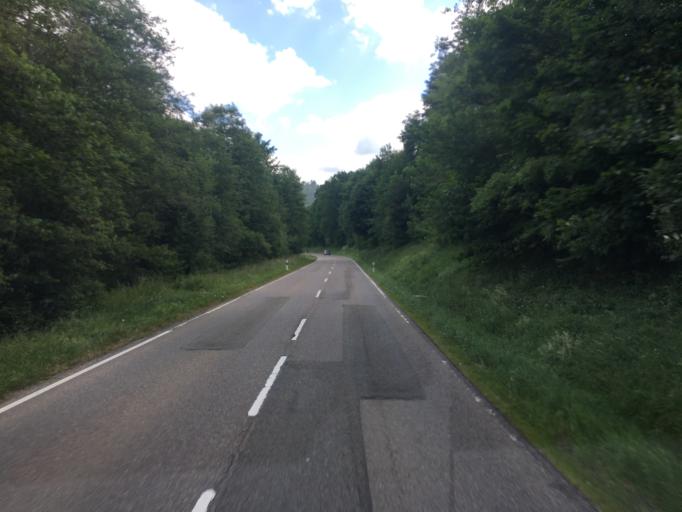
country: DE
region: Baden-Wuerttemberg
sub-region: Karlsruhe Region
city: Baiersbronn
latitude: 48.5190
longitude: 8.3892
